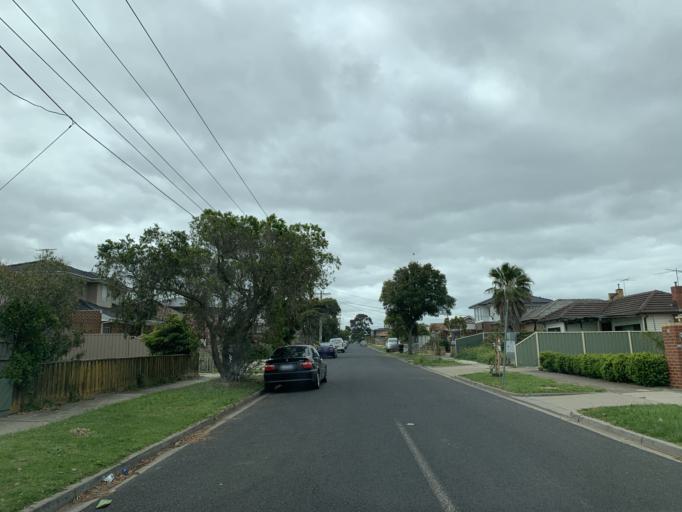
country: AU
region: Victoria
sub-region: Brimbank
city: St Albans
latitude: -37.7436
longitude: 144.8063
